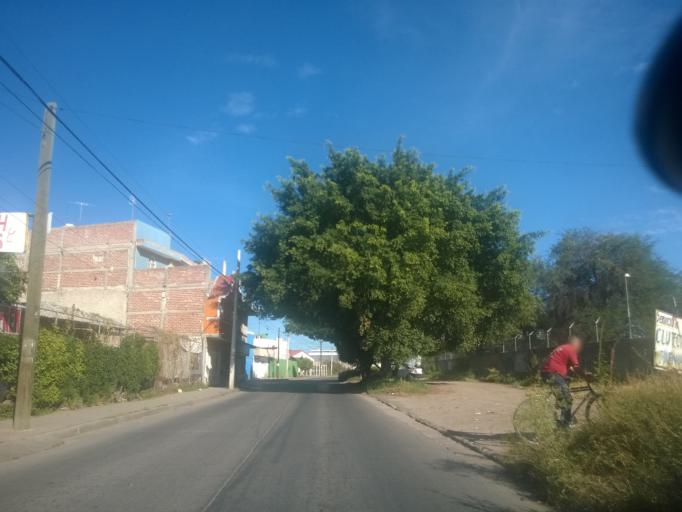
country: MX
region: Guanajuato
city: Leon
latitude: 21.1251
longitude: -101.6513
